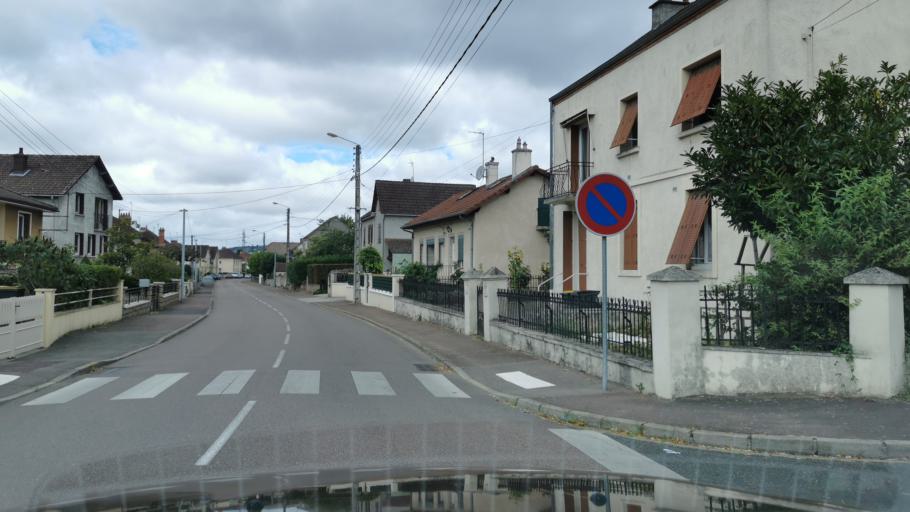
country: FR
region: Bourgogne
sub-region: Departement de Saone-et-Loire
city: Le Breuil
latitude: 46.8047
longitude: 4.4653
